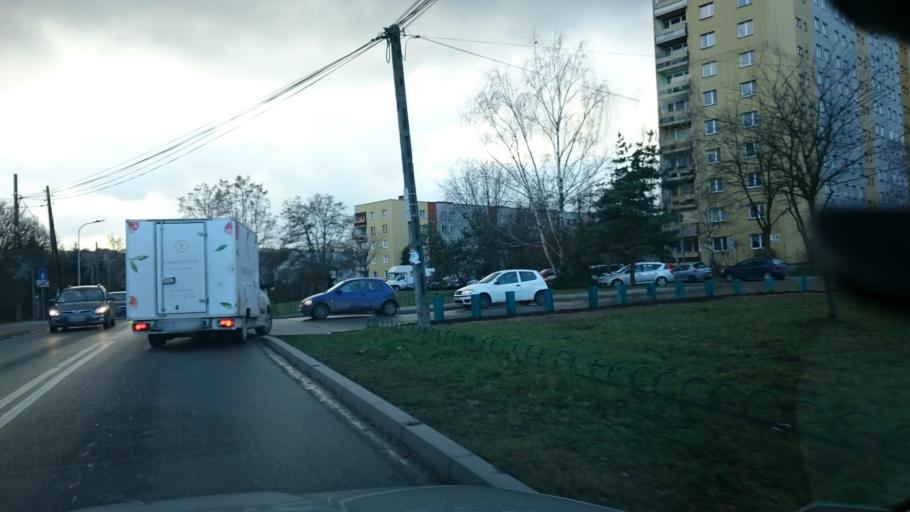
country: PL
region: Lesser Poland Voivodeship
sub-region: Powiat wielicki
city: Czarnochowice
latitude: 50.0093
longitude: 20.0219
